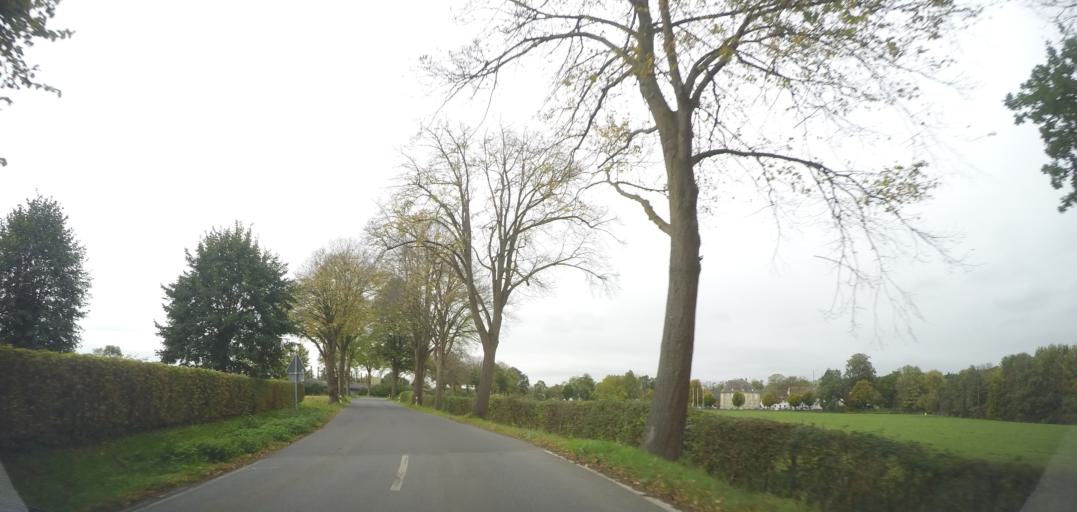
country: DE
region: North Rhine-Westphalia
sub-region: Regierungsbezirk Arnsberg
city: Bad Sassendorf
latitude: 51.6332
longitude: 8.1941
